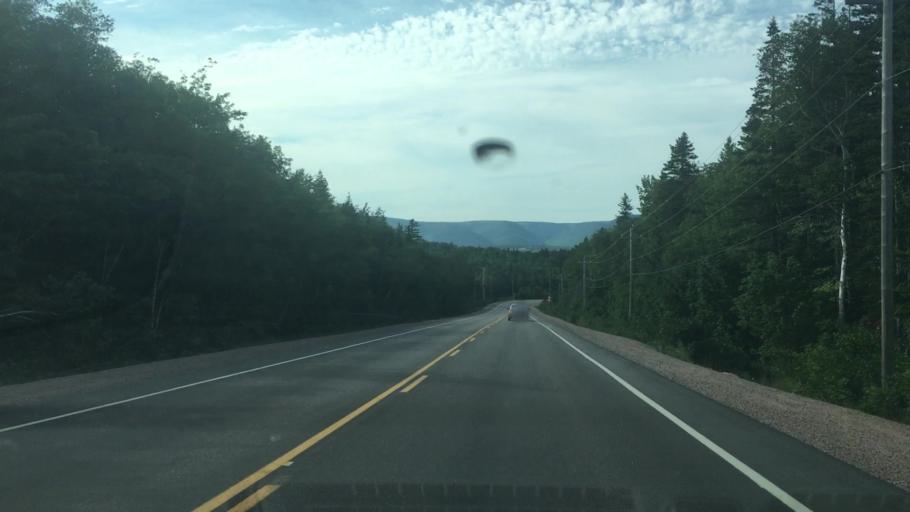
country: CA
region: Nova Scotia
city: Sydney Mines
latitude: 46.8563
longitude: -60.4589
